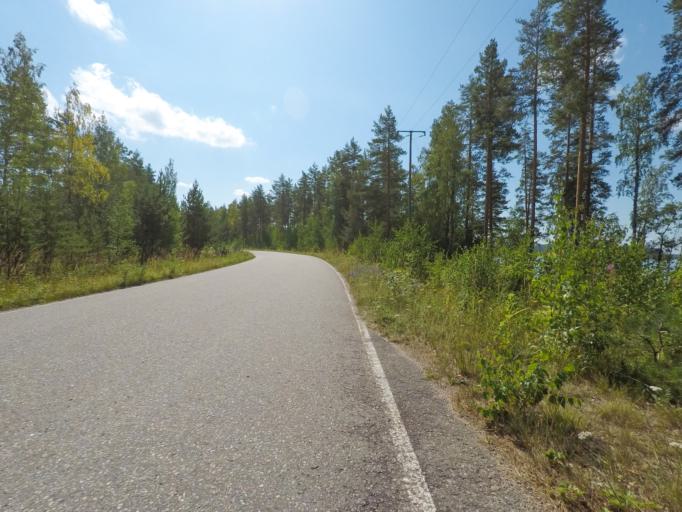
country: FI
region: Southern Savonia
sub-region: Mikkeli
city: Puumala
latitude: 61.5032
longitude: 28.1670
